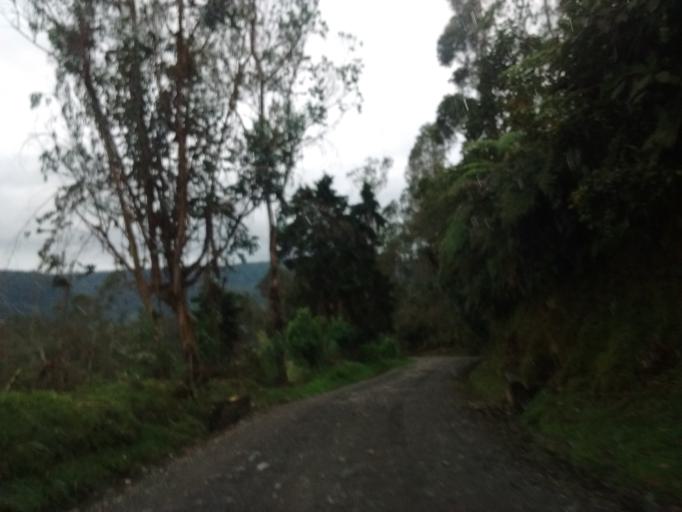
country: CO
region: Huila
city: La Argentina
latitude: 2.2607
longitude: -76.1963
